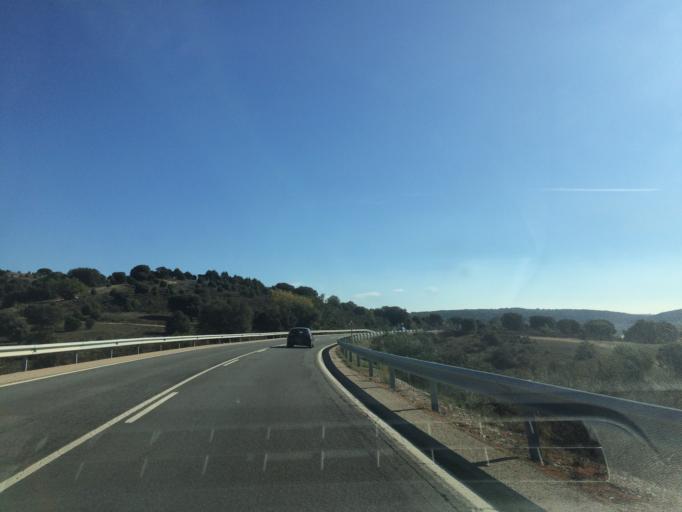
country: ES
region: Madrid
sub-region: Provincia de Madrid
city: Guadalix de la Sierra
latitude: 40.7828
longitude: -3.6606
